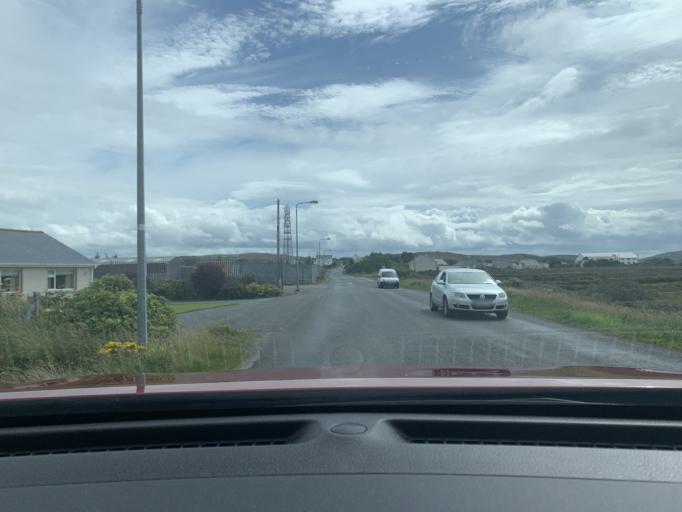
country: IE
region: Ulster
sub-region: County Donegal
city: Dungloe
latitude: 54.9572
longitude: -8.3648
